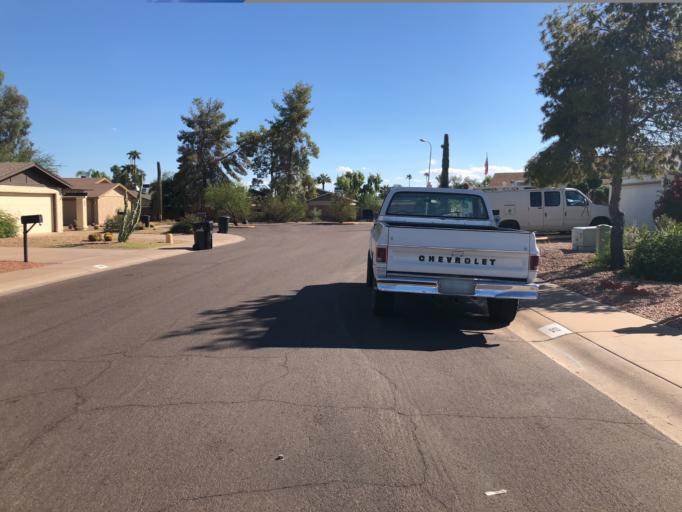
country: US
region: Arizona
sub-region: Maricopa County
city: Tempe
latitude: 33.4571
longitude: -111.8944
